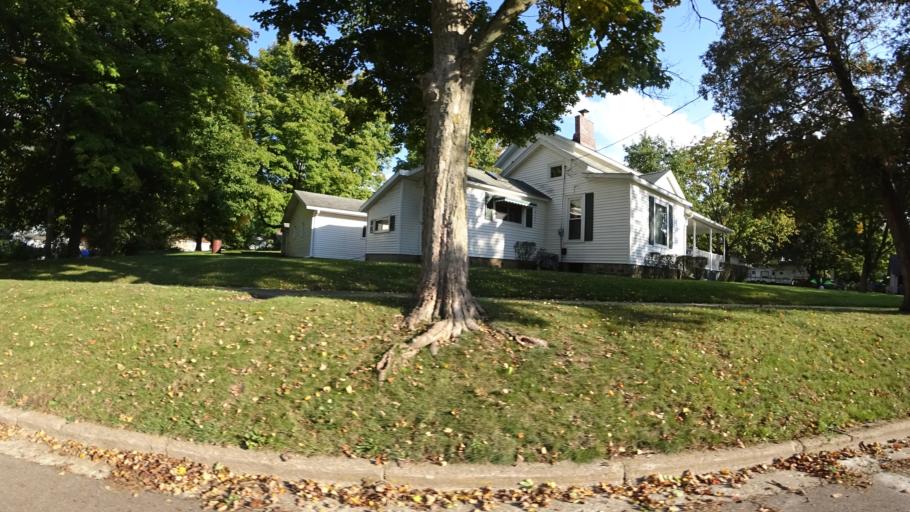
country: US
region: Michigan
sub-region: Saint Joseph County
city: Three Rivers
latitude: 41.9459
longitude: -85.6282
